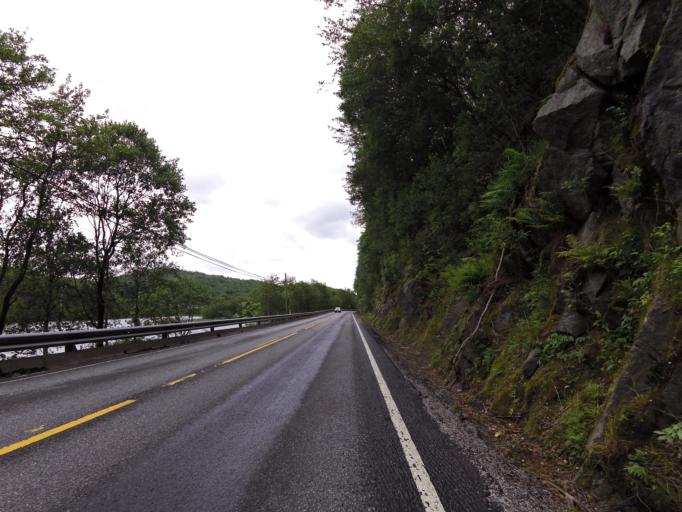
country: NO
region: Vest-Agder
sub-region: Farsund
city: Farsund
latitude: 58.1083
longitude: 6.9232
